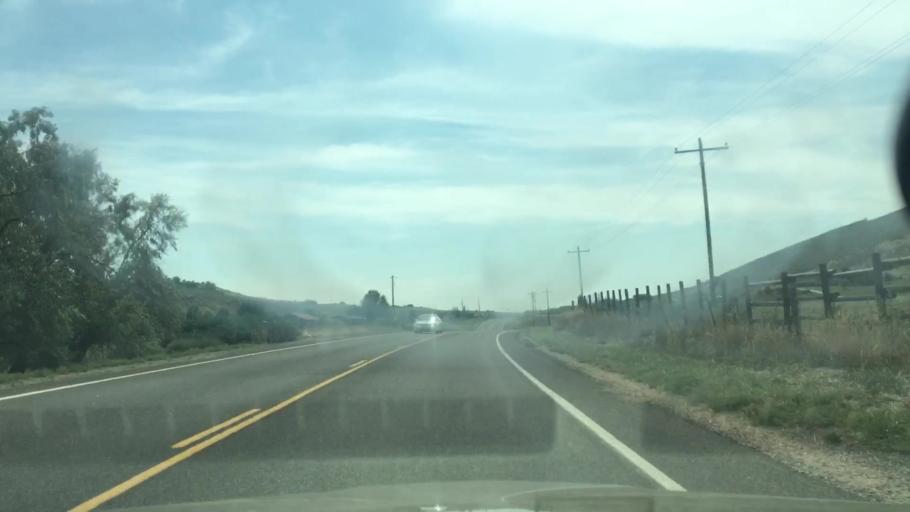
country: US
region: Colorado
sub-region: Larimer County
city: Campion
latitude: 40.3671
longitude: -105.1891
